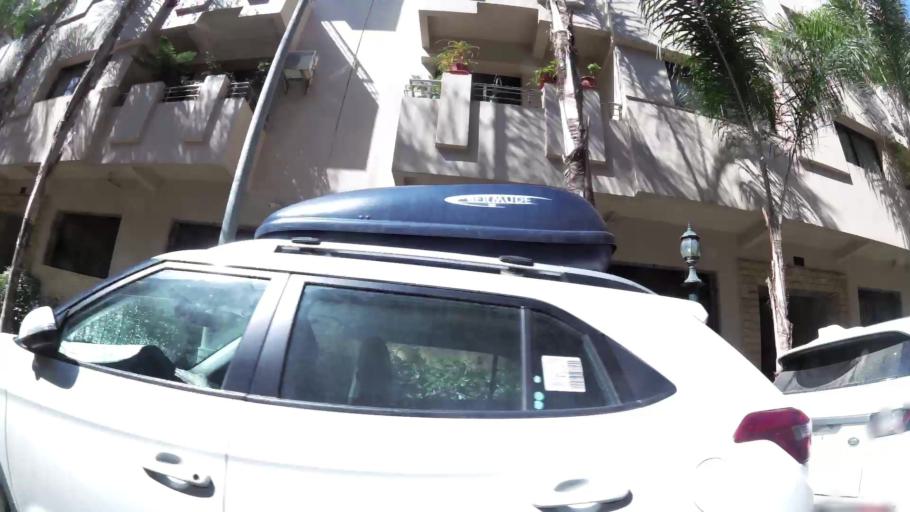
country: MA
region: Rabat-Sale-Zemmour-Zaer
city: Sale
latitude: 34.0633
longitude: -6.8004
